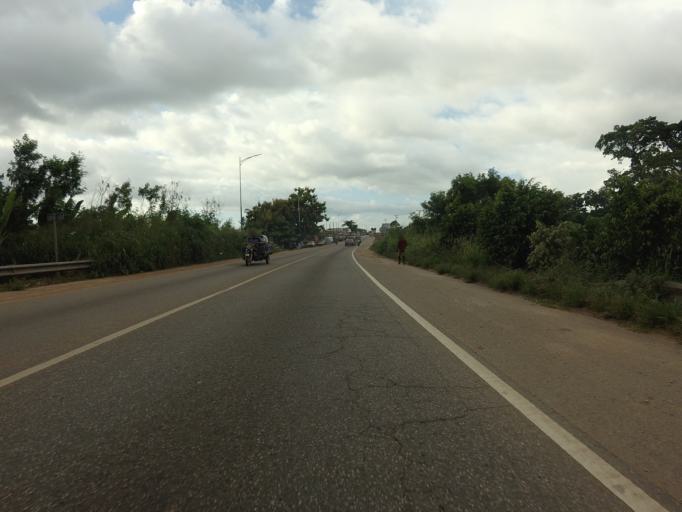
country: GH
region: Ashanti
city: Tafo
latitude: 6.8117
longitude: -1.6491
